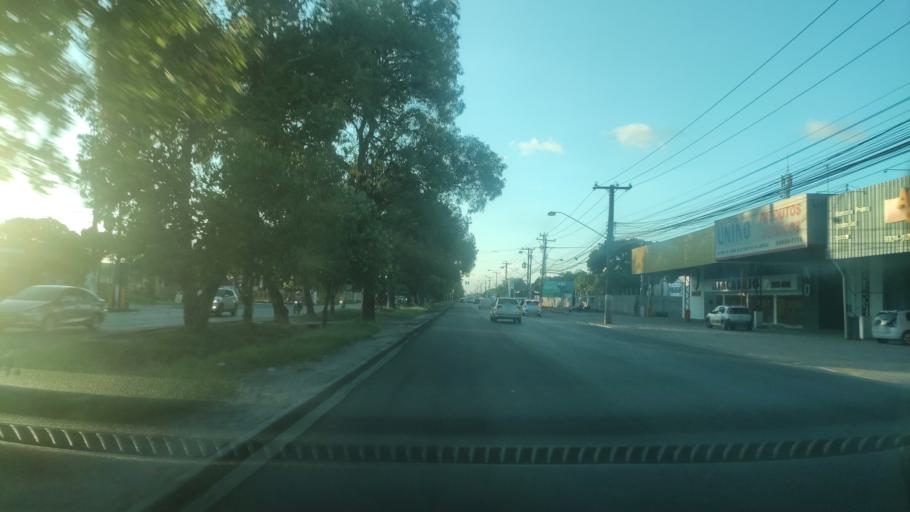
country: BR
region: Alagoas
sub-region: Satuba
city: Satuba
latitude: -9.5859
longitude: -35.7634
